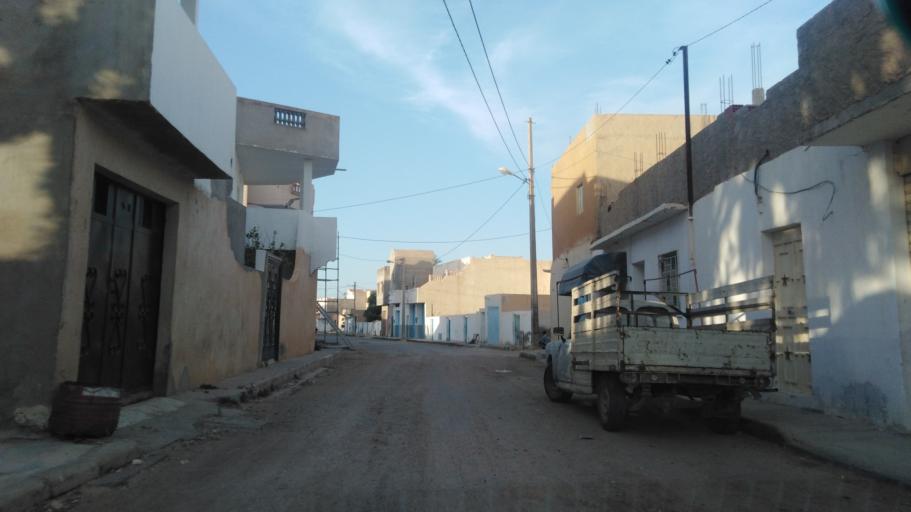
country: TN
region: Tataouine
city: Tataouine
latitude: 32.9390
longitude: 10.4558
